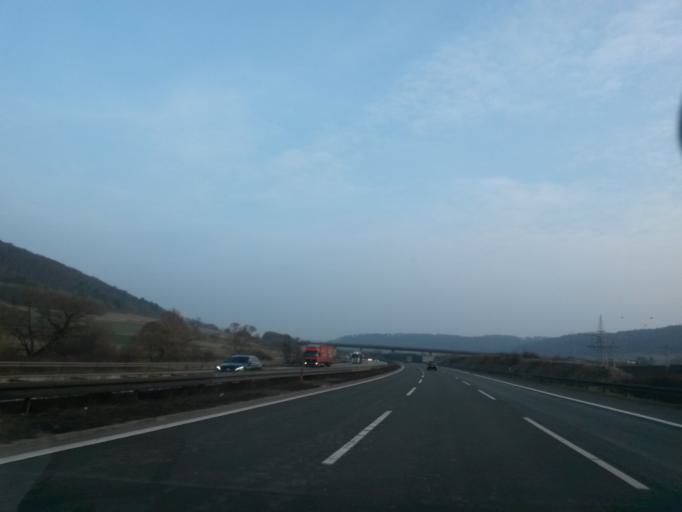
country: DE
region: Bavaria
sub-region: Regierungsbezirk Mittelfranken
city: Thalmassing
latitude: 49.0788
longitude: 11.2917
